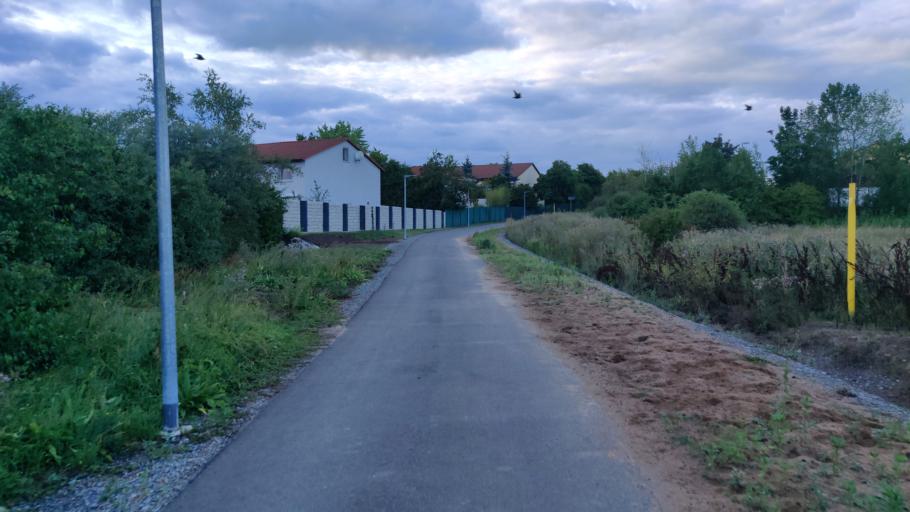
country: DE
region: Bavaria
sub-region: Regierungsbezirk Unterfranken
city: Niederwerrn
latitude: 50.0581
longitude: 10.1988
